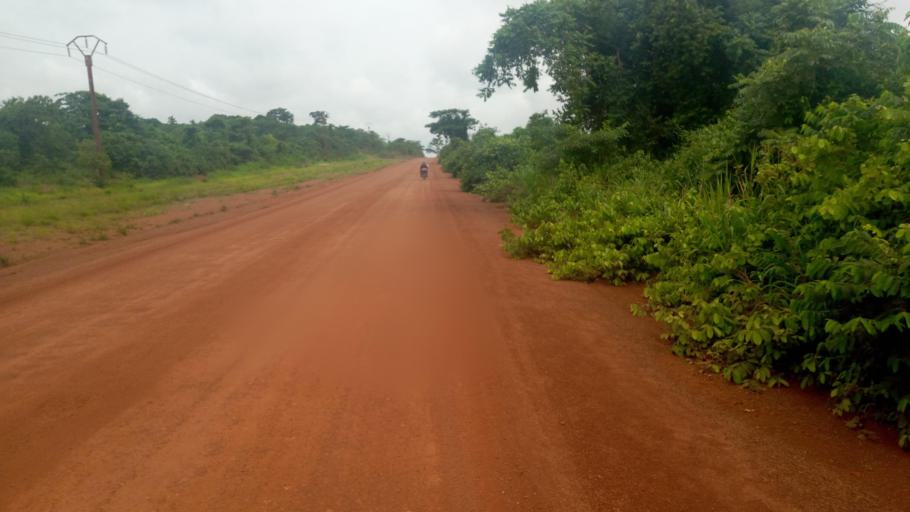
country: SL
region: Southern Province
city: Mogbwemo
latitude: 7.7386
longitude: -12.2826
